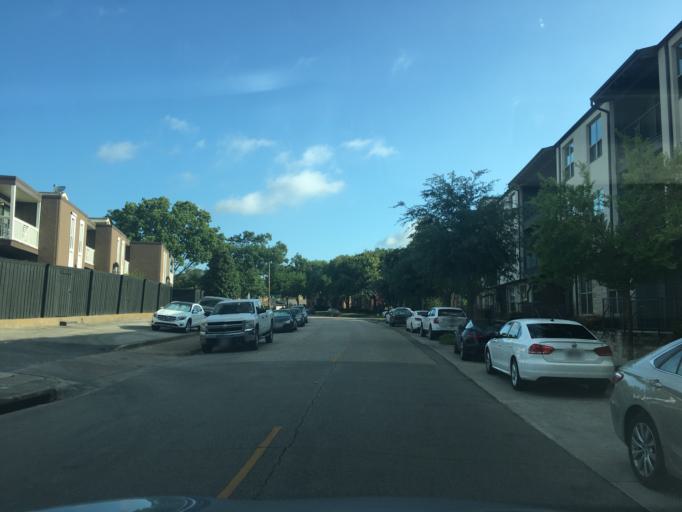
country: US
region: Texas
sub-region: Dallas County
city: Highland Park
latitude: 32.8436
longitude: -96.7628
